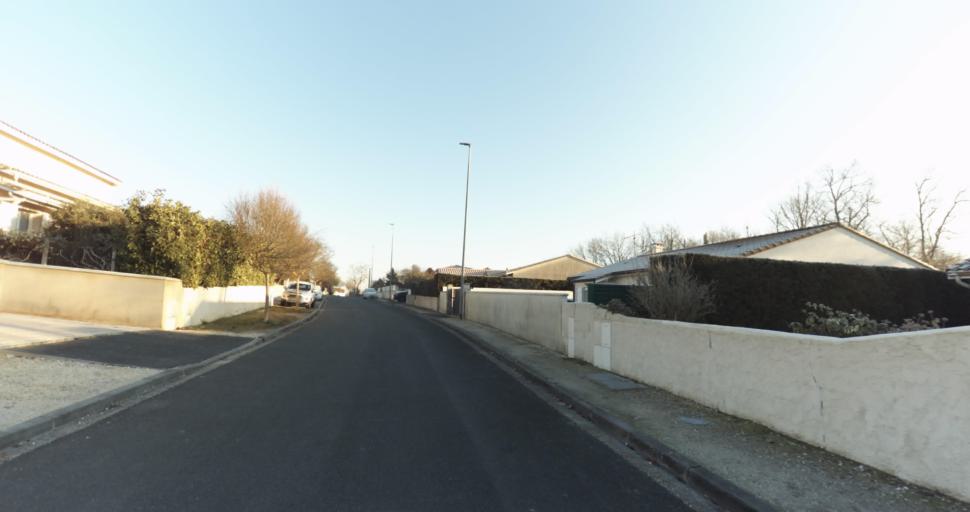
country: FR
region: Aquitaine
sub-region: Departement de la Gironde
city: Carbon-Blanc
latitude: 44.9086
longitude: -0.5001
